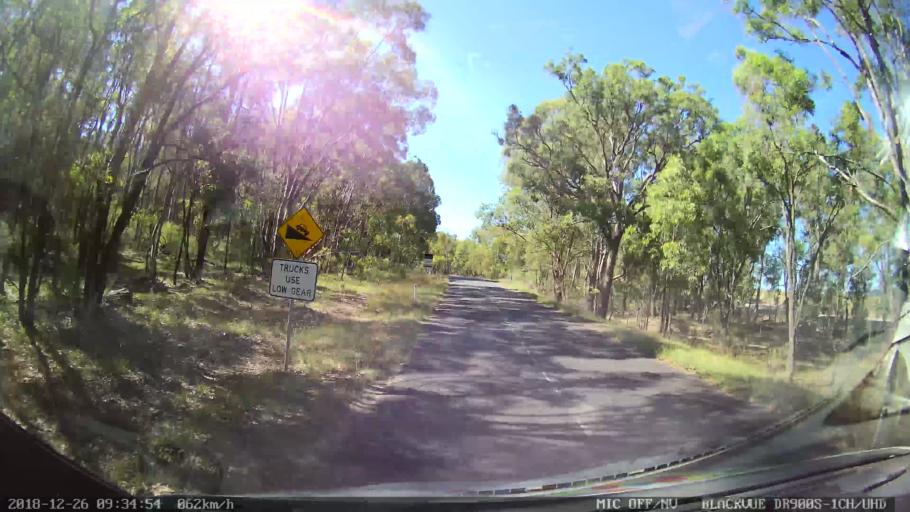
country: AU
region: New South Wales
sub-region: Mid-Western Regional
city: Kandos
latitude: -32.9099
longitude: 150.0383
